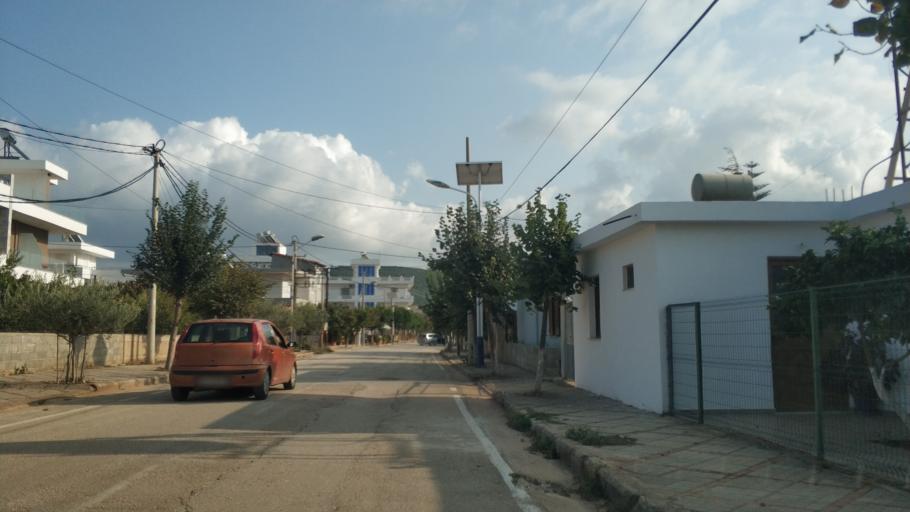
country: AL
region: Vlore
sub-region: Rrethi i Sarandes
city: Xarre
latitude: 39.7738
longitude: 20.0099
